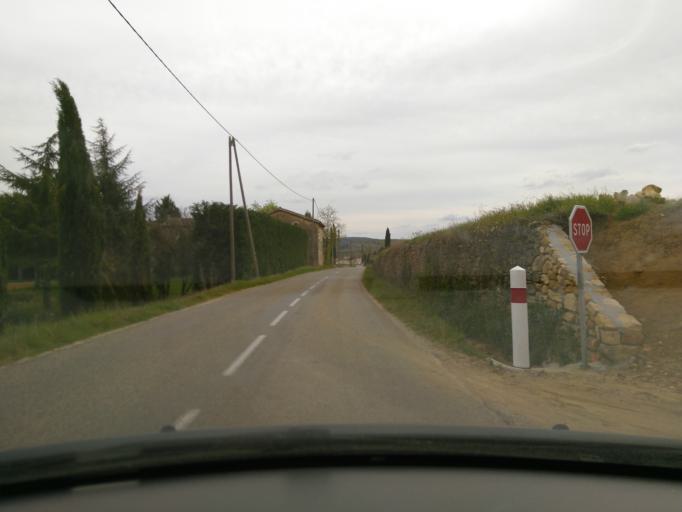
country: FR
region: Rhone-Alpes
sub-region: Departement de l'Ardeche
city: Ruoms
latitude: 44.4223
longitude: 4.4134
